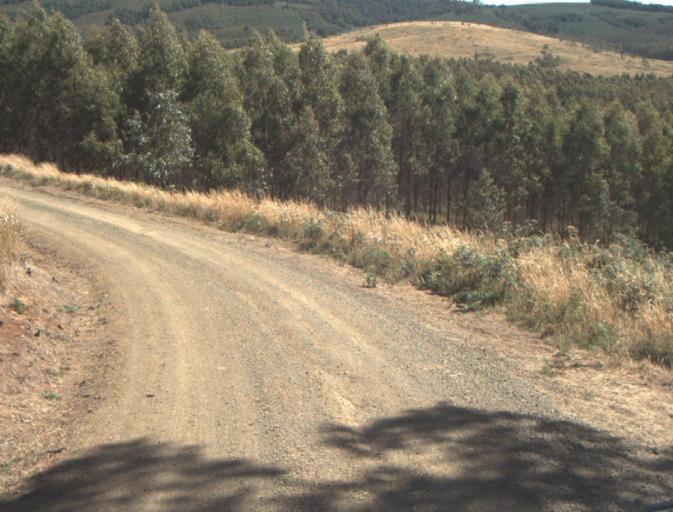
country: AU
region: Tasmania
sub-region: Dorset
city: Scottsdale
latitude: -41.3464
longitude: 147.4544
